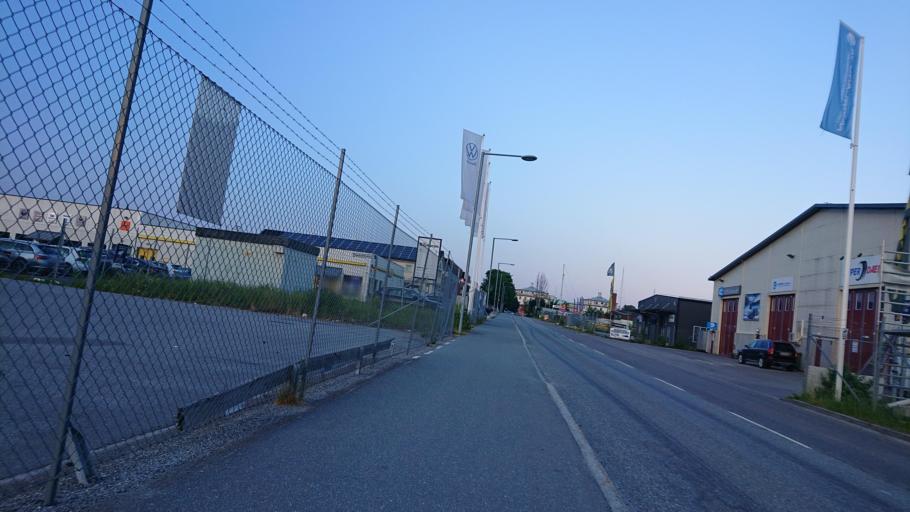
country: SE
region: Stockholm
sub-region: Osterakers Kommun
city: Akersberga
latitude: 59.4789
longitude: 18.2883
